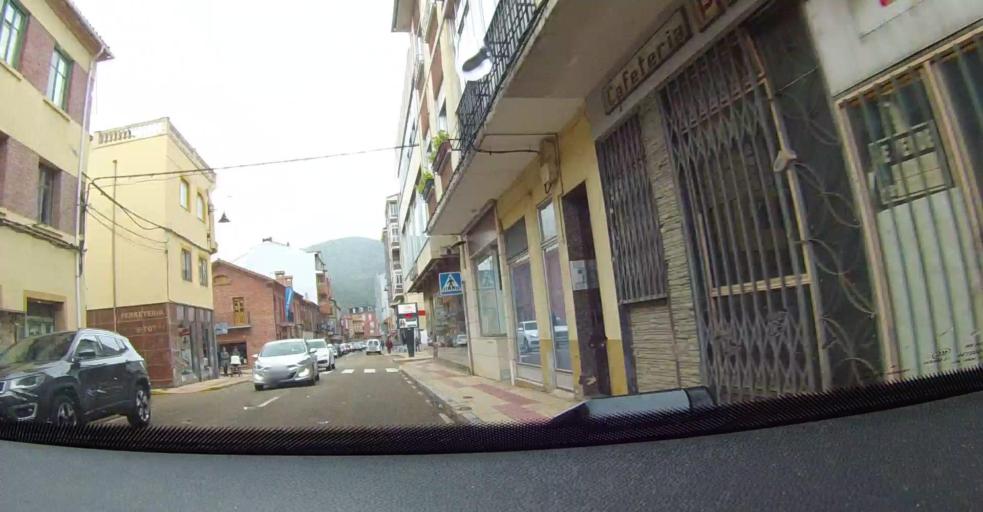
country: ES
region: Castille and Leon
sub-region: Provincia de Leon
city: Cistierna
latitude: 42.8024
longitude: -5.1271
